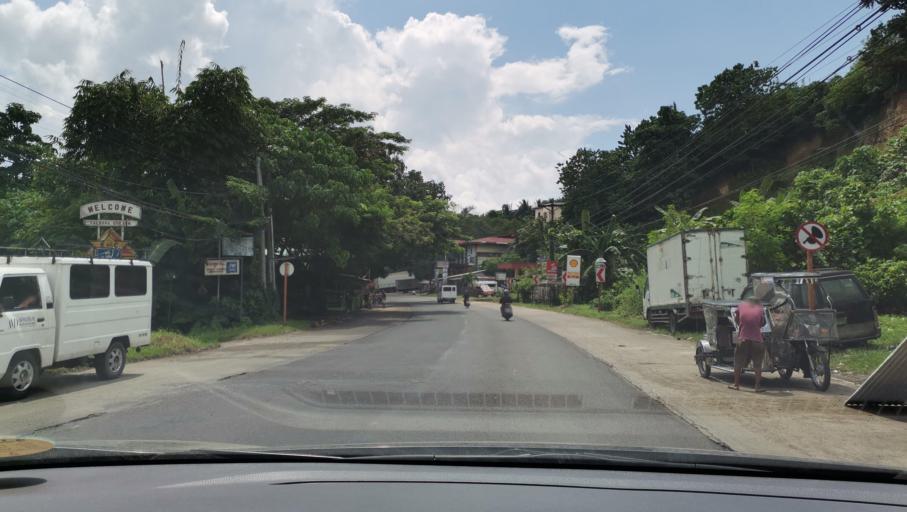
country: PH
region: Calabarzon
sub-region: Province of Quezon
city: Calauag
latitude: 13.9536
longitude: 122.2930
